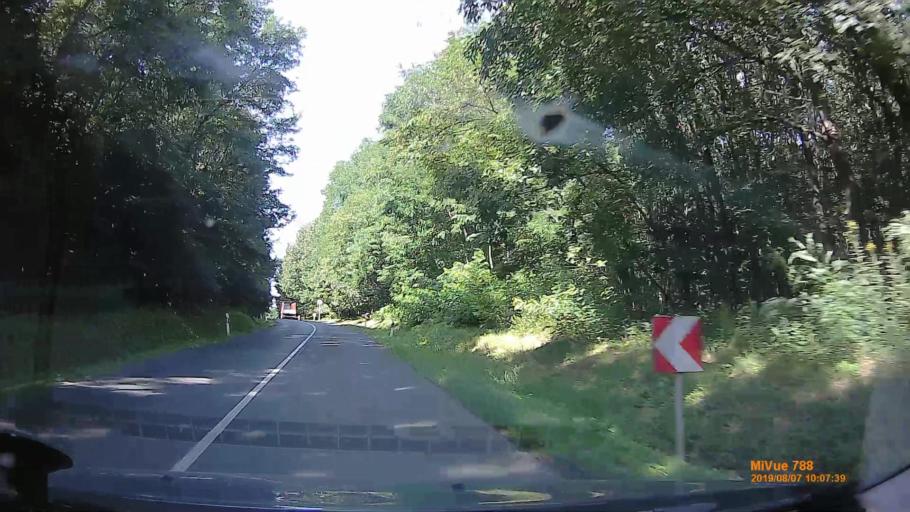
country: HU
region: Zala
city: Lenti
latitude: 46.6876
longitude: 16.7220
